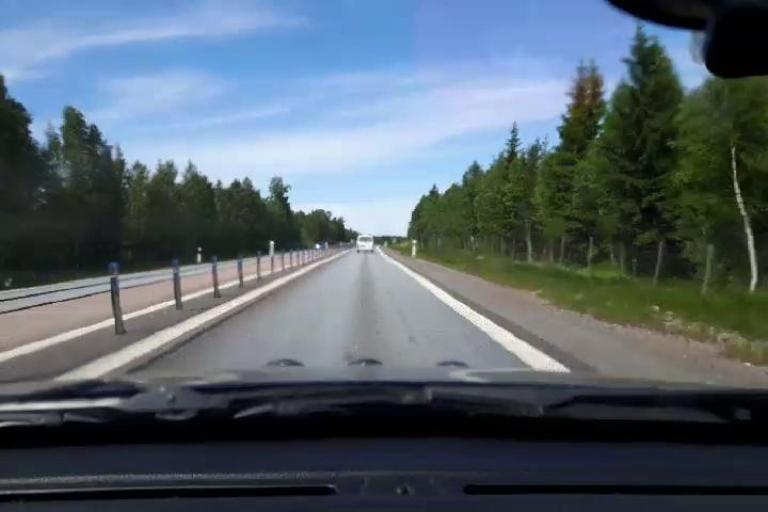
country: SE
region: Gaevleborg
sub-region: Gavle Kommun
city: Gavle
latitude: 60.8038
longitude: 17.0820
